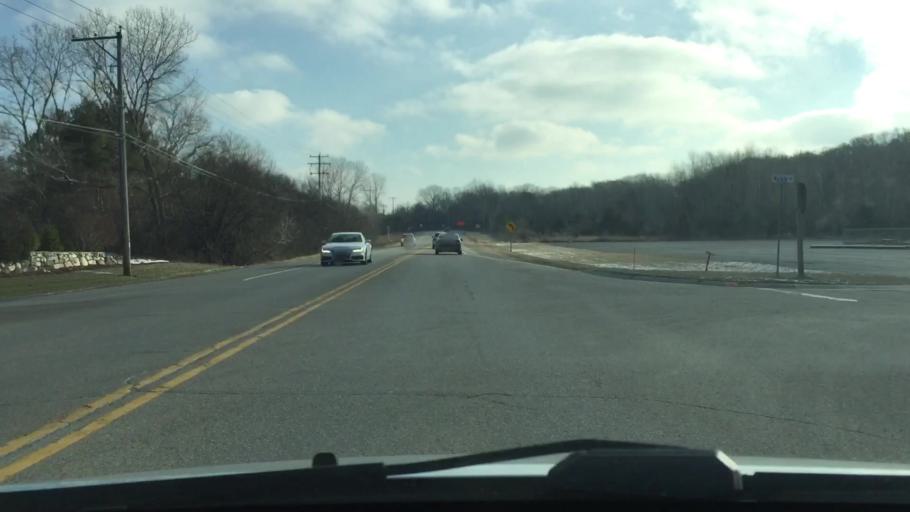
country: US
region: Wisconsin
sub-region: Waukesha County
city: Wales
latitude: 43.0117
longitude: -88.3938
